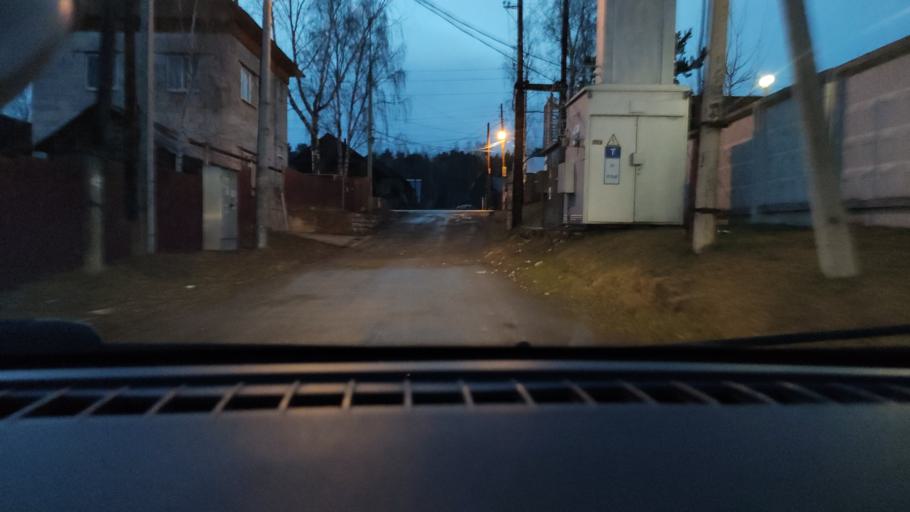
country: RU
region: Perm
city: Perm
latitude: 58.0338
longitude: 56.2490
